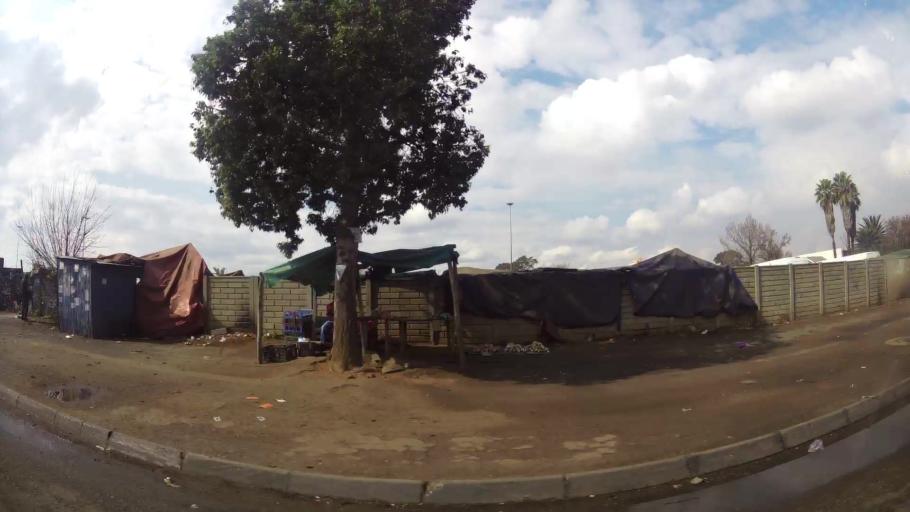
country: ZA
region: Gauteng
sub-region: Sedibeng District Municipality
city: Vereeniging
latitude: -26.6733
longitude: 27.9341
